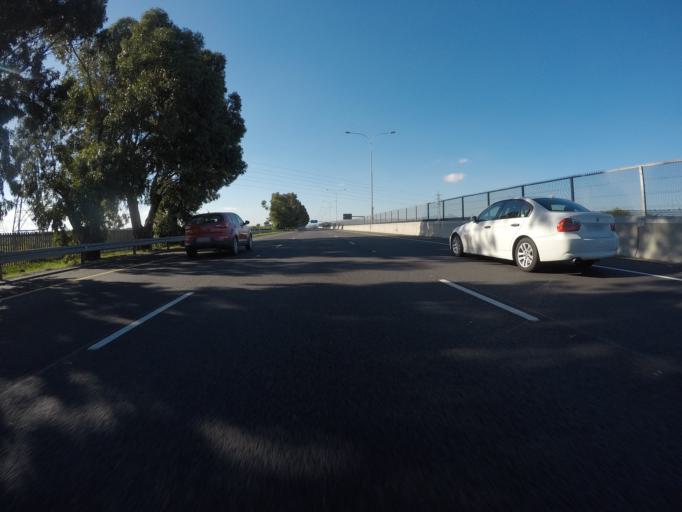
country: ZA
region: Western Cape
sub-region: City of Cape Town
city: Lansdowne
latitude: -33.9876
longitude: 18.6470
